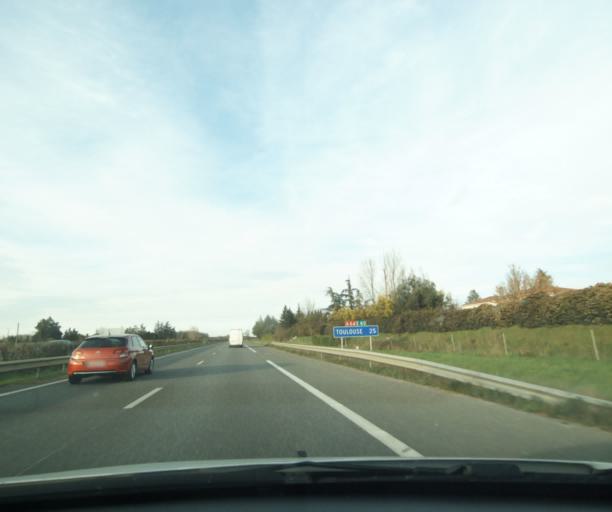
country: FR
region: Midi-Pyrenees
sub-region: Departement de la Haute-Garonne
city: Le Fauga
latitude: 43.4062
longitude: 1.2929
